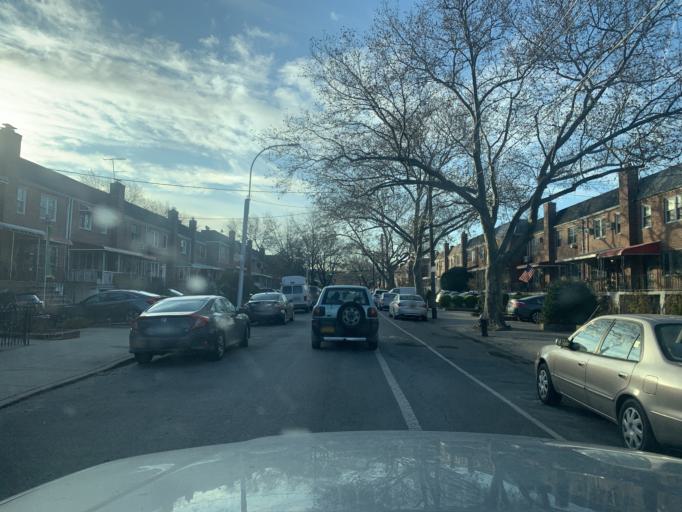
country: US
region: New York
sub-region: Queens County
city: Long Island City
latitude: 40.7581
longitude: -73.8925
